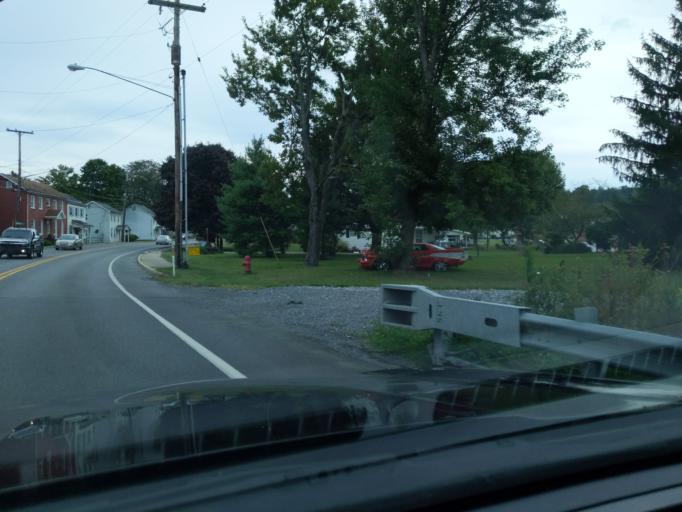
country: US
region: Pennsylvania
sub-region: Blair County
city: Duncansville
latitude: 40.3907
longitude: -78.4357
